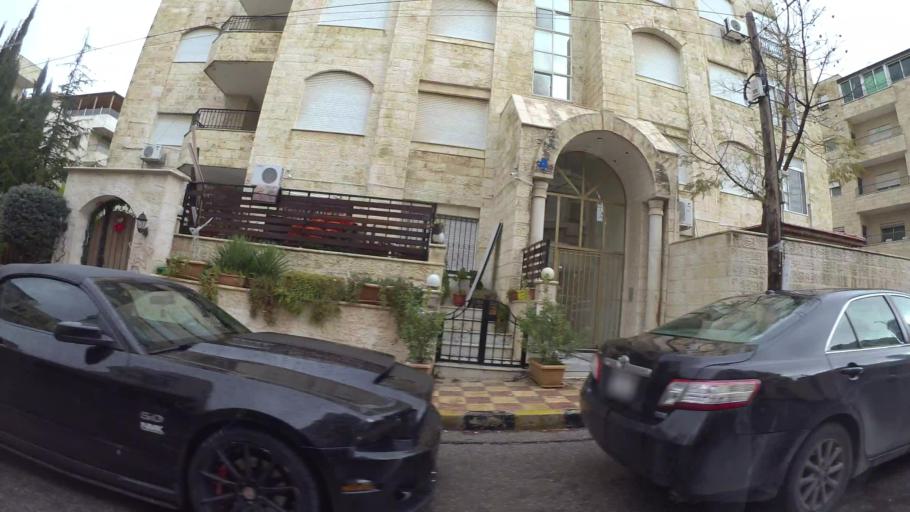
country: JO
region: Amman
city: Wadi as Sir
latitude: 31.9646
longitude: 35.8639
